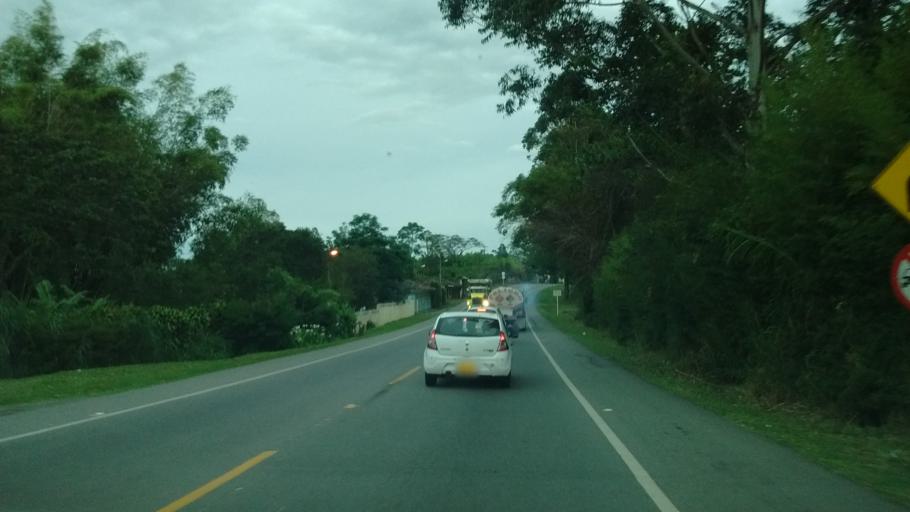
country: CO
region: Cauca
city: Cajibio
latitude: 2.6939
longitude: -76.5313
